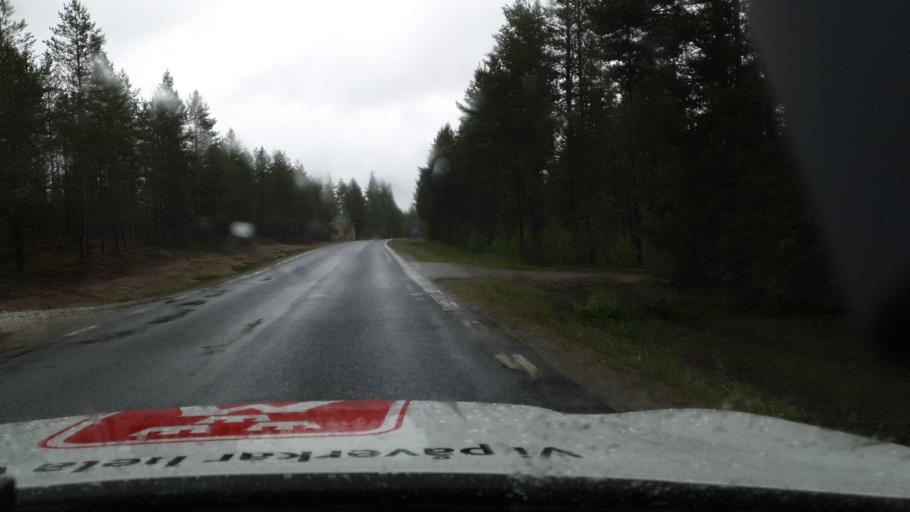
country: SE
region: Vaesterbotten
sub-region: Asele Kommun
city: Asele
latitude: 64.1816
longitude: 17.3534
